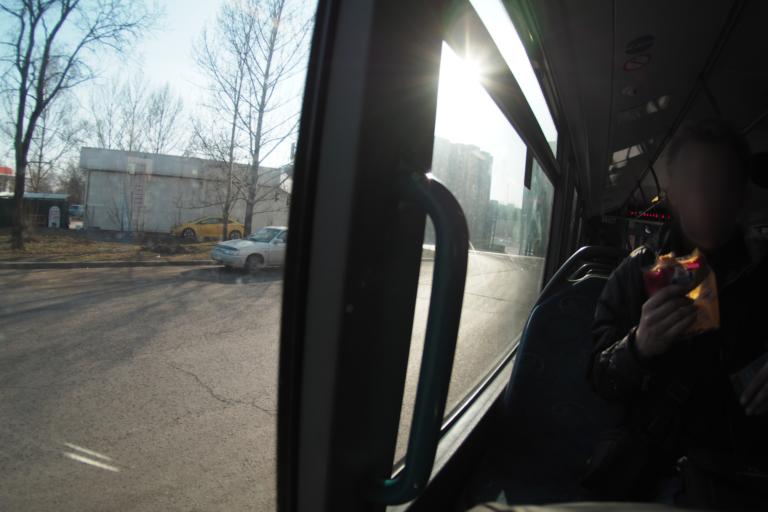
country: RU
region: Moscow
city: Matveyevskoye
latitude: 55.7079
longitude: 37.4840
